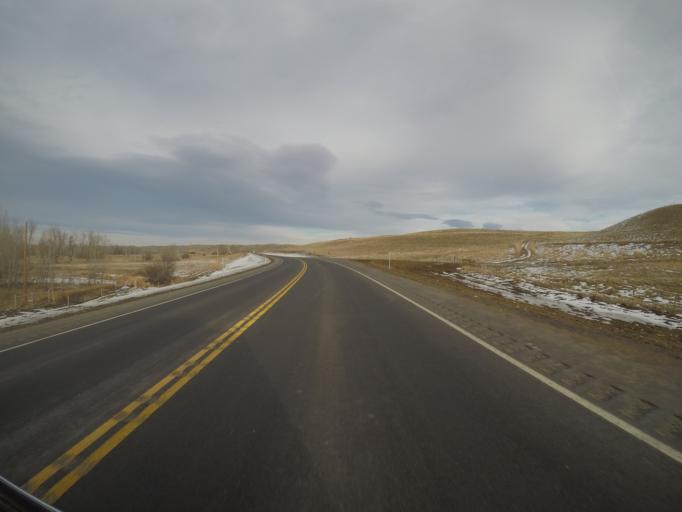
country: US
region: Montana
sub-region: Stillwater County
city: Absarokee
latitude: 45.4359
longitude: -109.4604
